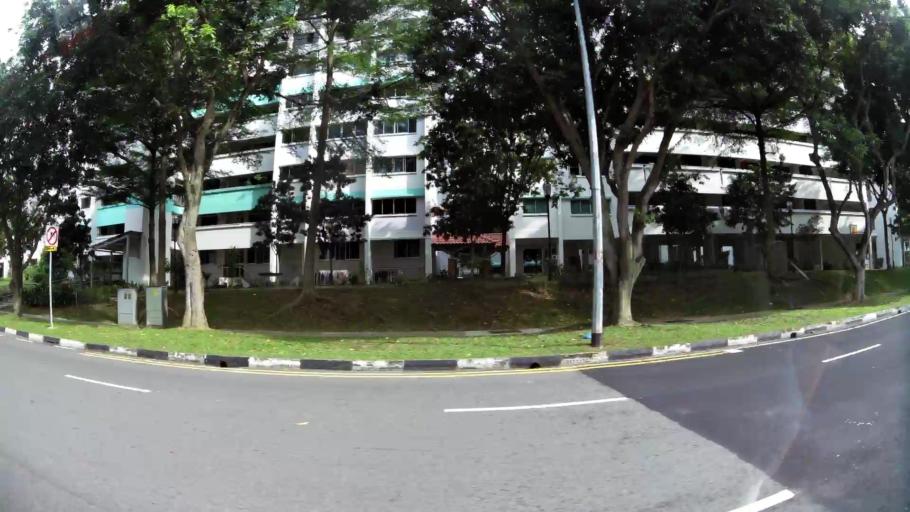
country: SG
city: Singapore
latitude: 1.3725
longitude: 103.8863
